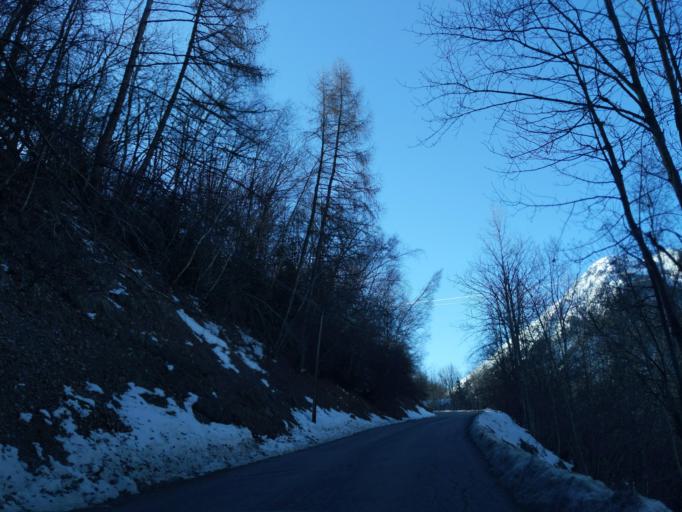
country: FR
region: Rhone-Alpes
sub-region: Departement de la Savoie
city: Saint-Martin-de-Belleville
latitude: 45.4168
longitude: 6.4954
